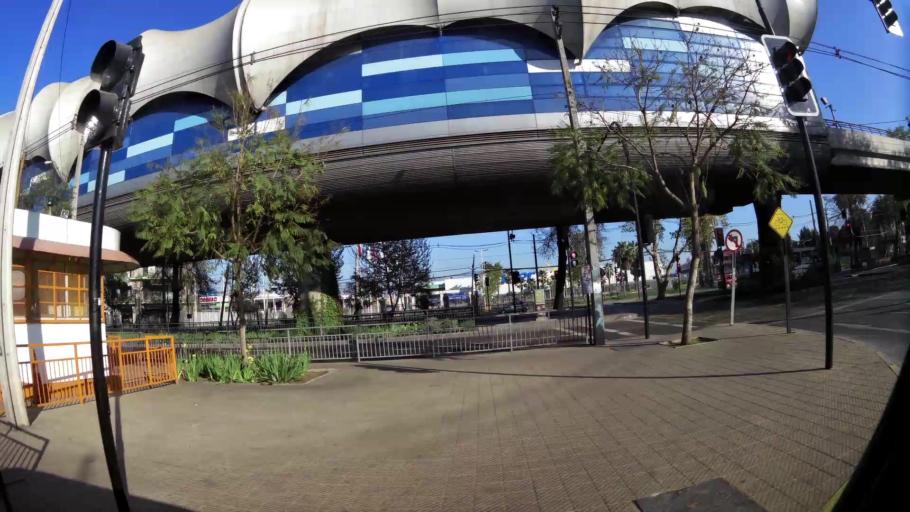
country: CL
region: Santiago Metropolitan
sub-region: Provincia de Santiago
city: Lo Prado
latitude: -33.4818
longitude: -70.7449
